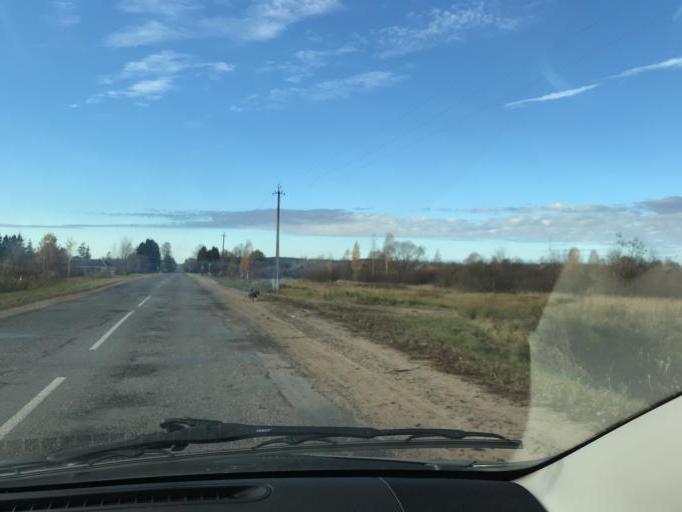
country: BY
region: Vitebsk
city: Haradok
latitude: 55.3734
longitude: 29.6306
